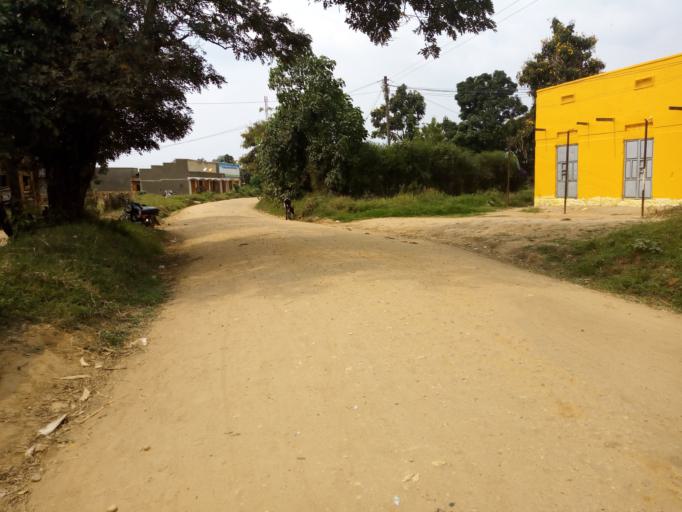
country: UG
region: Western Region
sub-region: Kanungu District
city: Ntungamo
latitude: -0.7475
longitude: 29.6948
